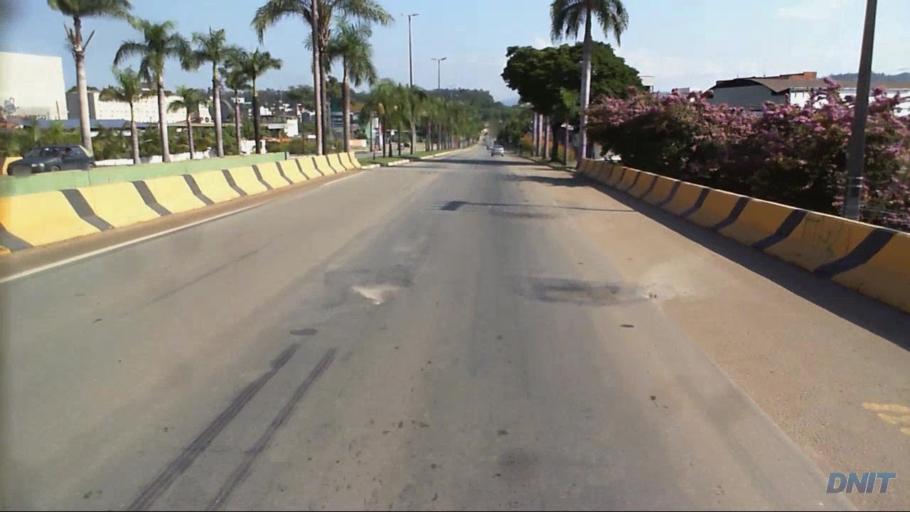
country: BR
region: Minas Gerais
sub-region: Ipatinga
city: Ipatinga
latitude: -19.4647
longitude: -42.5349
